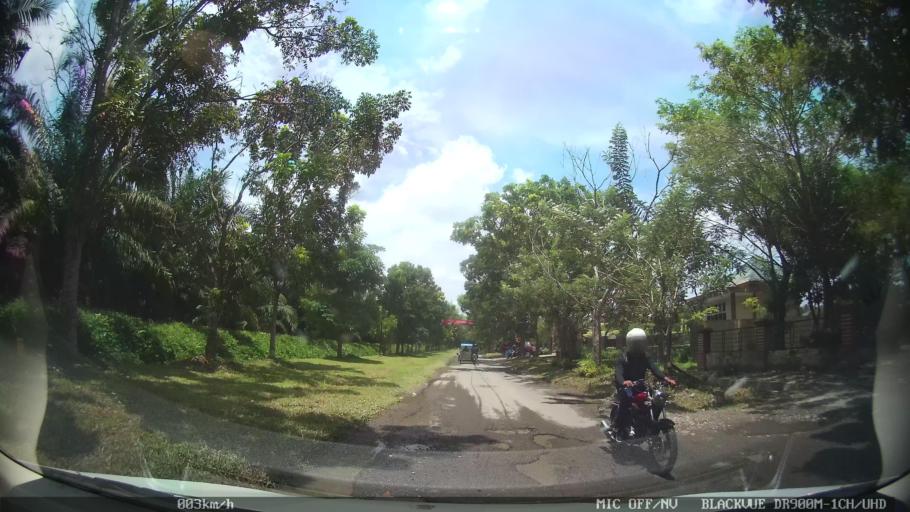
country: ID
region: North Sumatra
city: Percut
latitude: 3.5404
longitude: 98.8726
